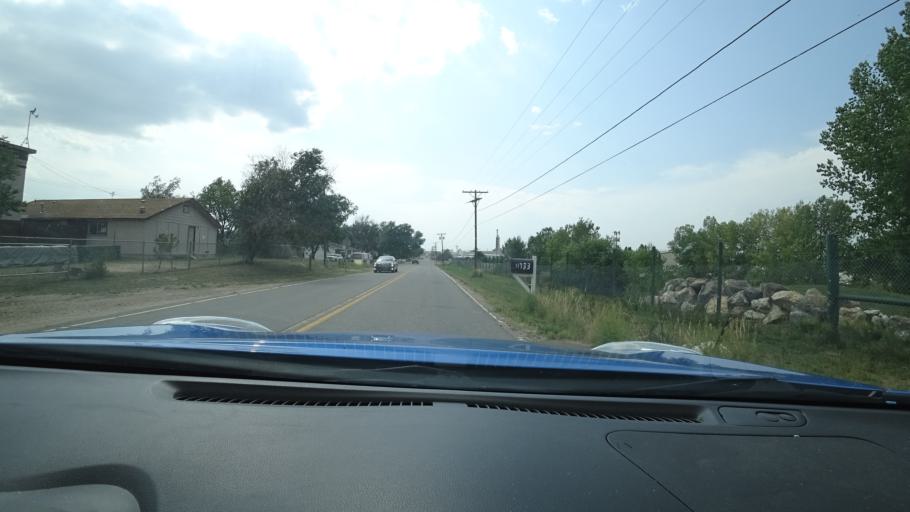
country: US
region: Colorado
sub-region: Adams County
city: Todd Creek
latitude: 39.9217
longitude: -104.8468
